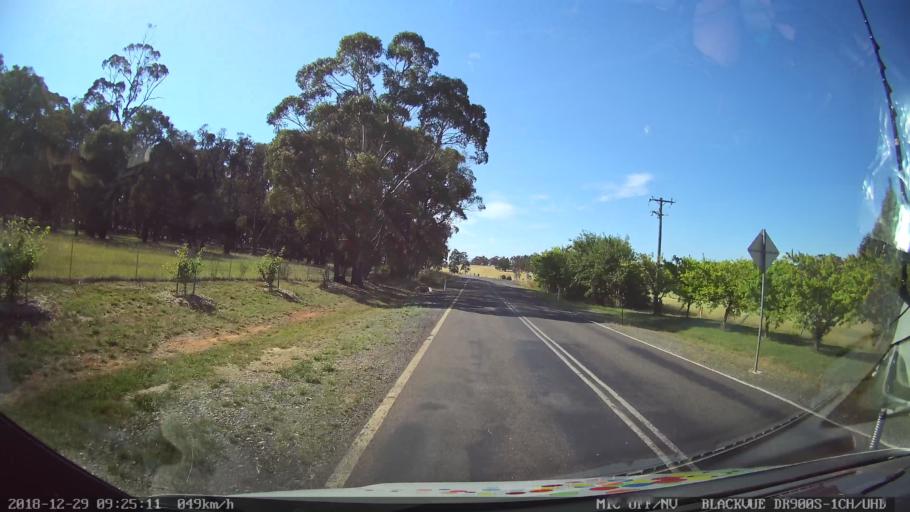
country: AU
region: New South Wales
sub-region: Upper Lachlan Shire
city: Crookwell
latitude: -34.5419
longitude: 149.3939
